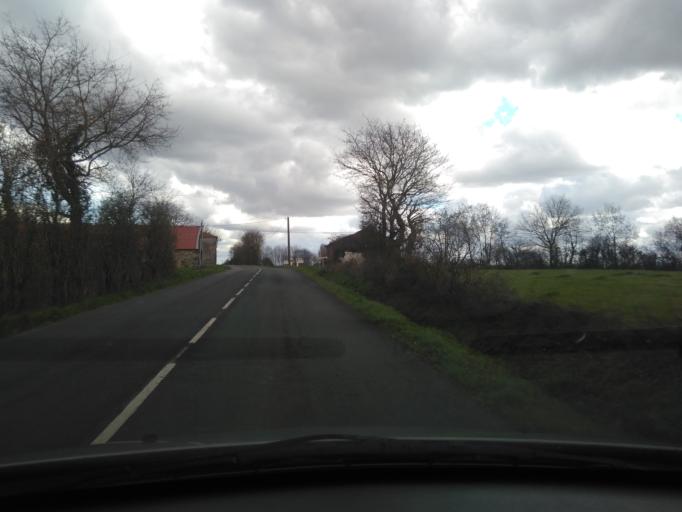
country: FR
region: Pays de la Loire
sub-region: Departement de la Vendee
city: Les Essarts
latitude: 46.7486
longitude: -1.2075
